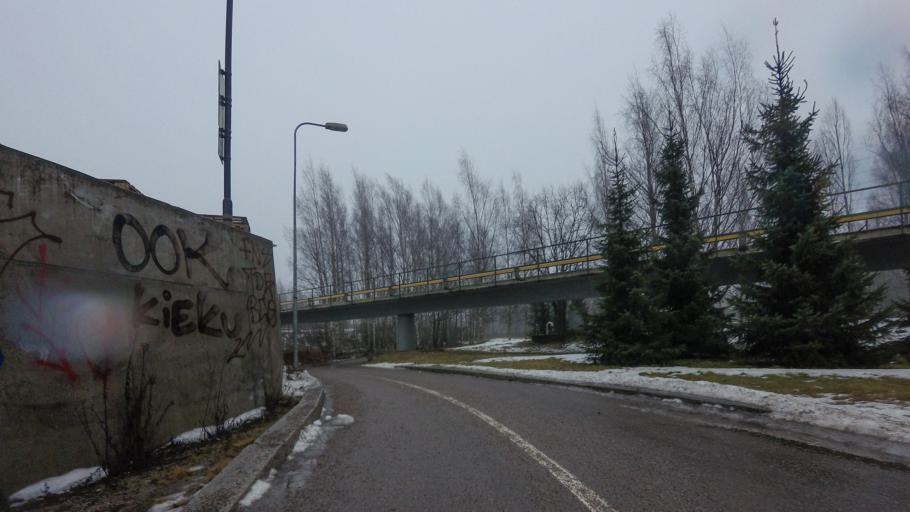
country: FI
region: Uusimaa
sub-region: Helsinki
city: Vantaa
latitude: 60.2090
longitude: 25.0630
